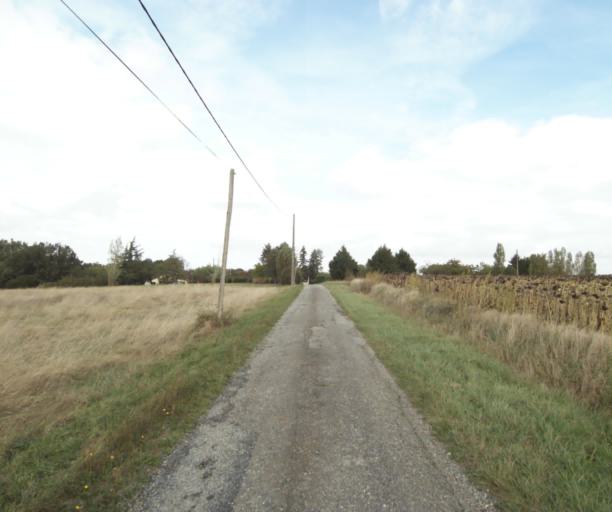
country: FR
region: Midi-Pyrenees
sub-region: Departement du Tarn-et-Garonne
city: Beaumont-de-Lomagne
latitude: 43.8735
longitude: 1.0939
